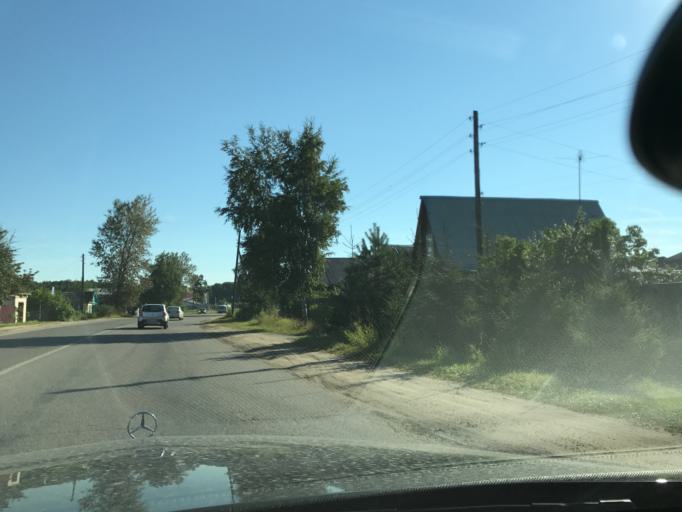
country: RU
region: Moskovskaya
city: Chernogolovka
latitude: 56.0020
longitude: 38.3662
